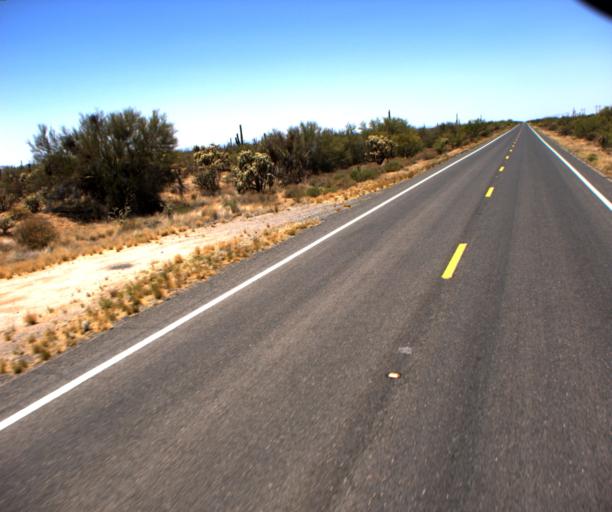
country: US
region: Arizona
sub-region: Pinal County
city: Florence
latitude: 32.8153
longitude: -111.1970
